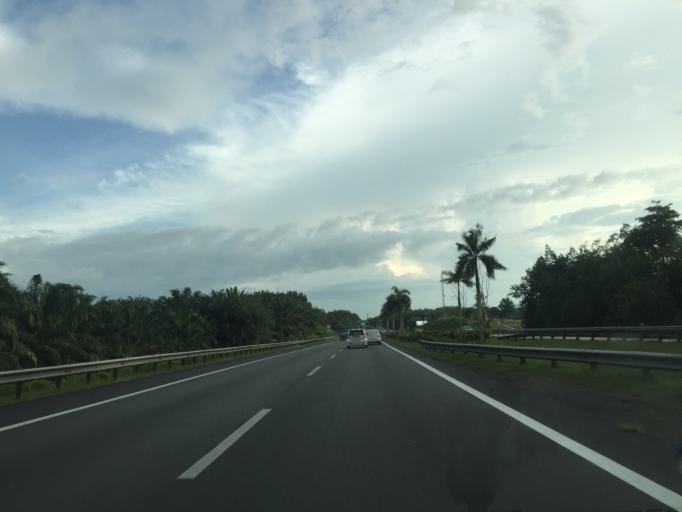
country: MY
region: Kedah
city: Gurun
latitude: 5.8480
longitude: 100.4853
